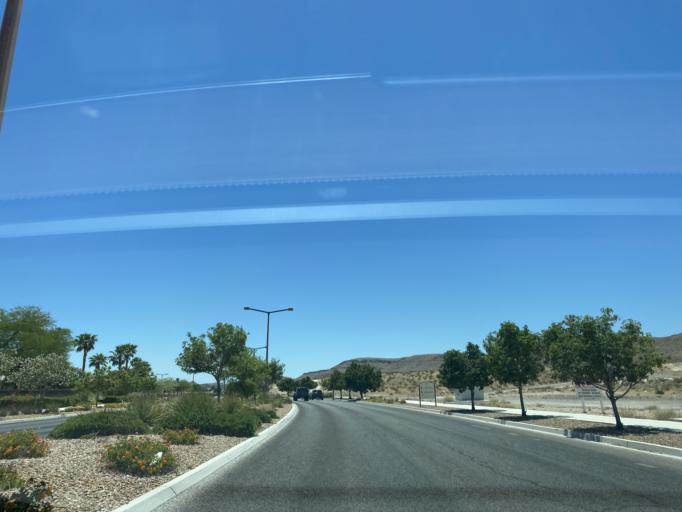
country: US
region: Nevada
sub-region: Clark County
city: Summerlin South
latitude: 36.1036
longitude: -115.3277
